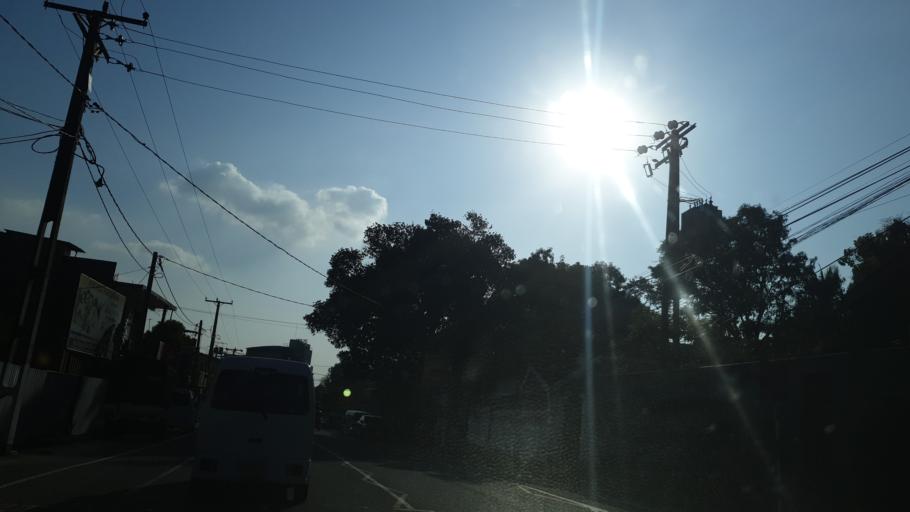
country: LK
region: Western
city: Sri Jayewardenepura Kotte
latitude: 6.8553
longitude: 79.8877
